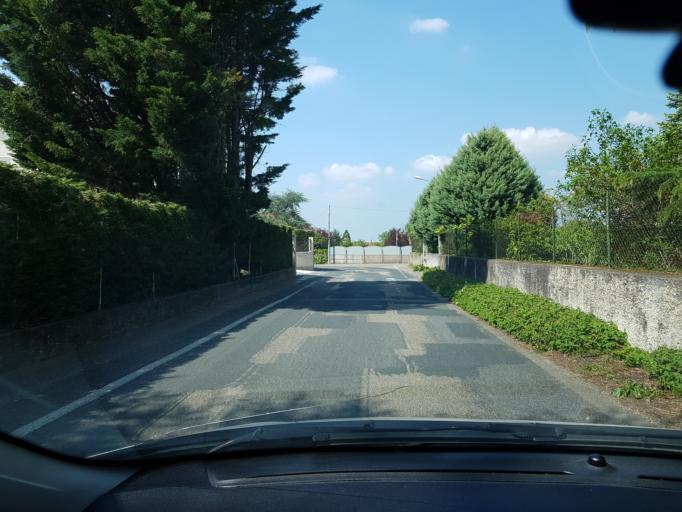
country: FR
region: Rhone-Alpes
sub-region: Departement du Rhone
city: Taluyers
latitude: 45.6383
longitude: 4.7200
